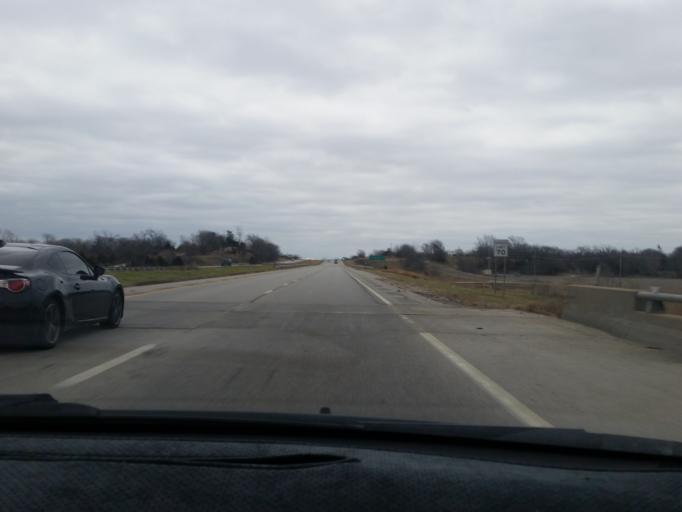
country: US
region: Kansas
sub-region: Douglas County
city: Eudora
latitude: 38.9429
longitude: -95.0626
